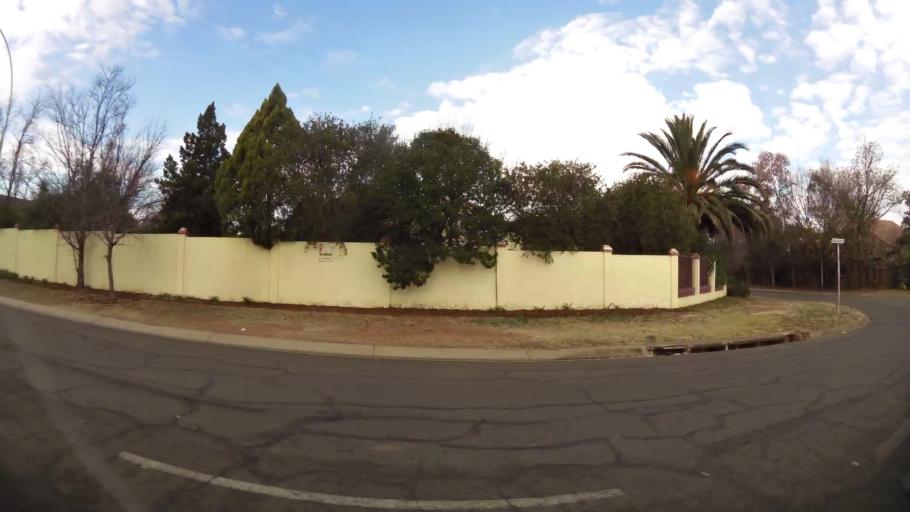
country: ZA
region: Orange Free State
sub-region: Mangaung Metropolitan Municipality
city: Bloemfontein
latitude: -29.0802
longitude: 26.1964
